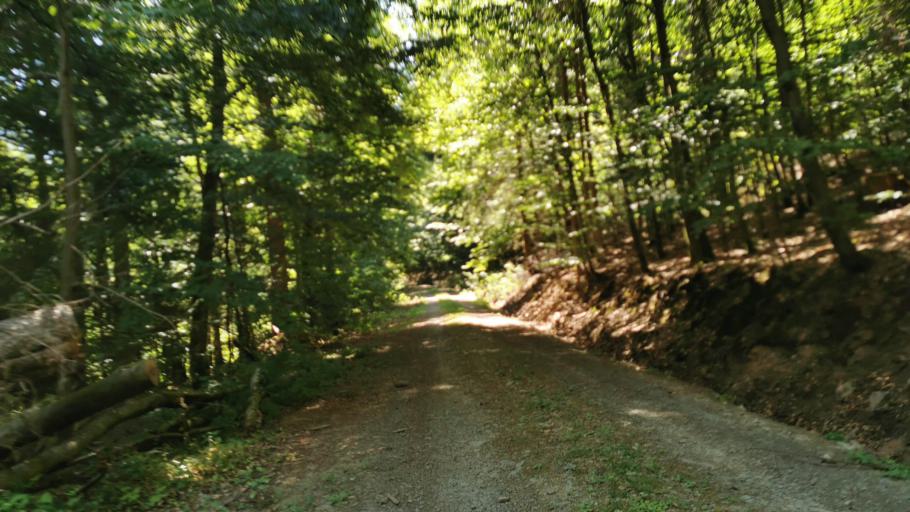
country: DE
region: Bavaria
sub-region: Upper Franconia
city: Pressig
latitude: 50.3922
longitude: 11.2937
